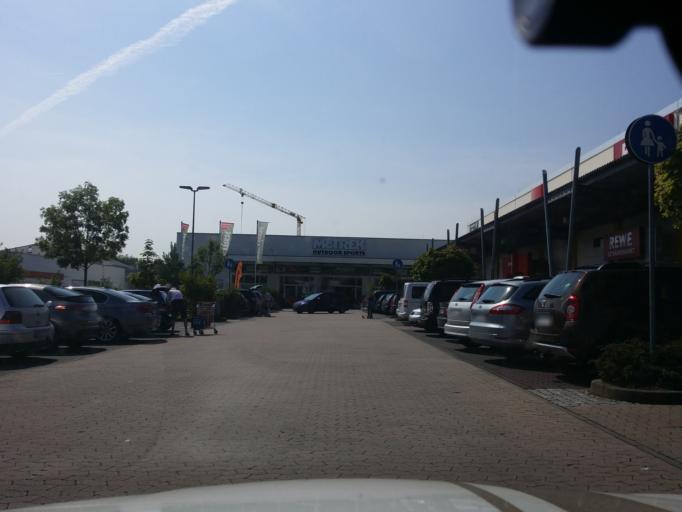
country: DE
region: Hesse
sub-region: Regierungsbezirk Darmstadt
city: Idstein
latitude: 50.2263
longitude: 8.2644
